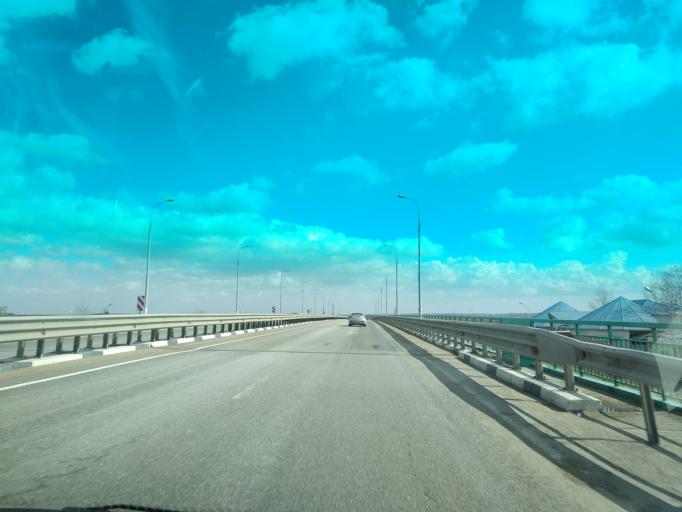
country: RU
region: Krasnodarskiy
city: Goryachiy Klyuch
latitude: 44.6444
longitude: 39.1279
